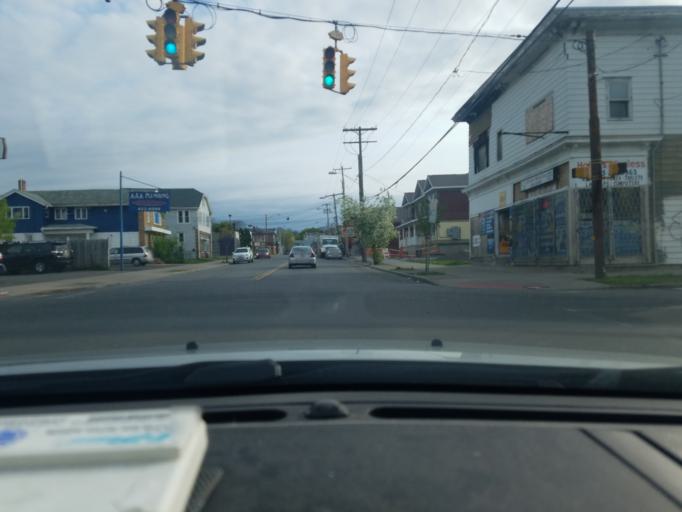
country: US
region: New York
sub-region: Onondaga County
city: Syracuse
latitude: 43.0617
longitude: -76.1449
